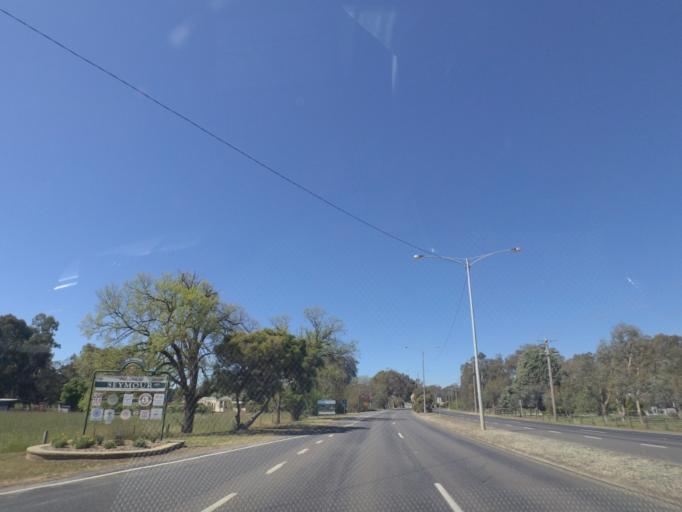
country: AU
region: Victoria
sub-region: Murrindindi
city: Kinglake West
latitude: -37.0222
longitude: 145.1165
